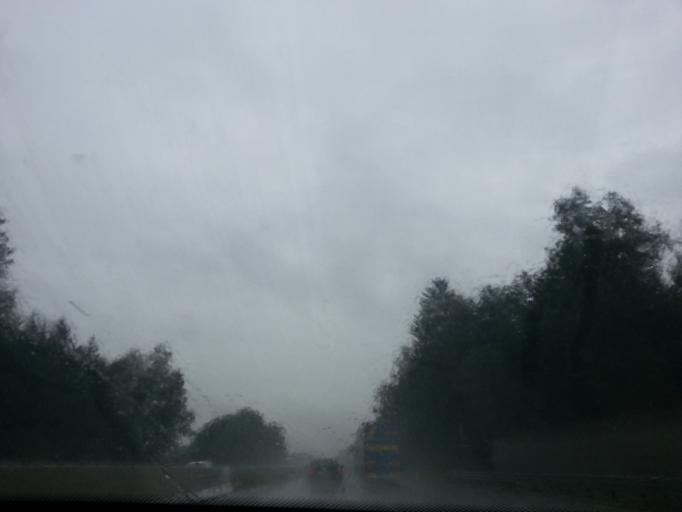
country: AT
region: Upper Austria
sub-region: Politischer Bezirk Gmunden
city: Laakirchen
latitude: 48.0042
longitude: 13.8580
